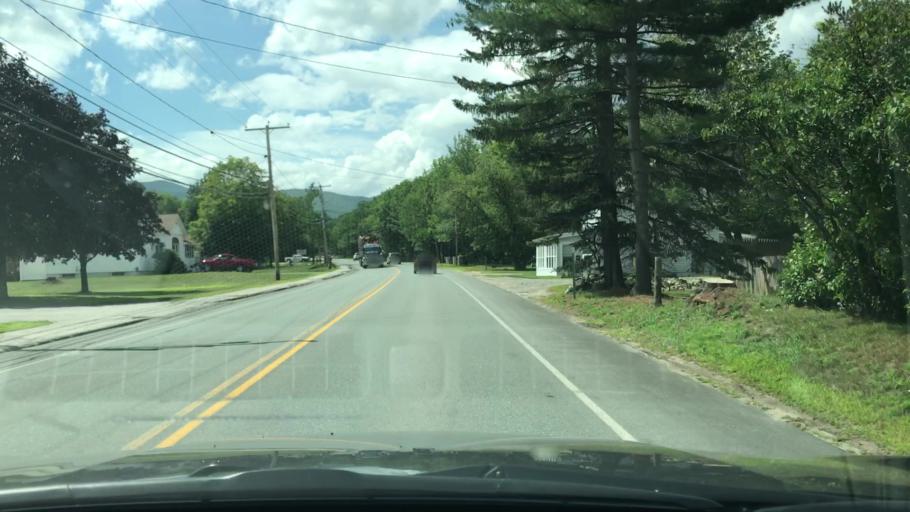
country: US
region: New Hampshire
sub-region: Coos County
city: Gorham
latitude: 44.3990
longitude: -71.2068
